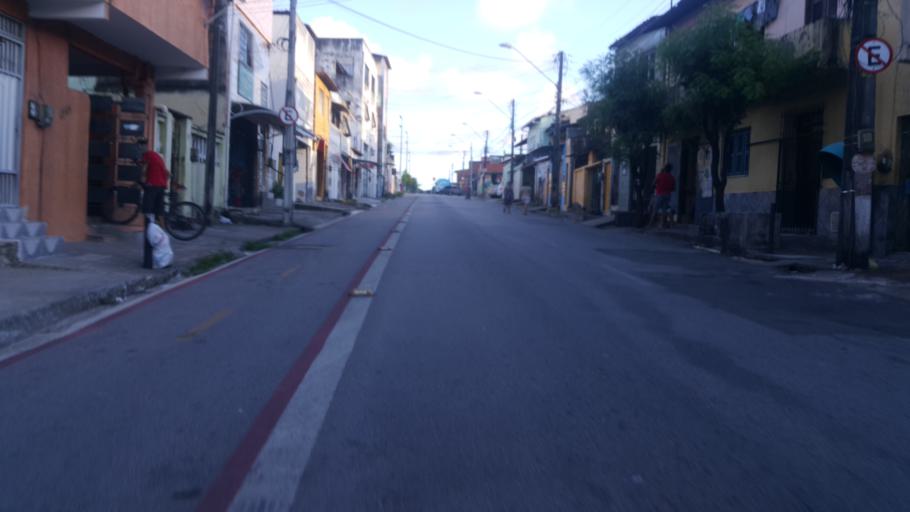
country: BR
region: Ceara
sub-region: Fortaleza
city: Fortaleza
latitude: -3.7507
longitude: -38.5396
